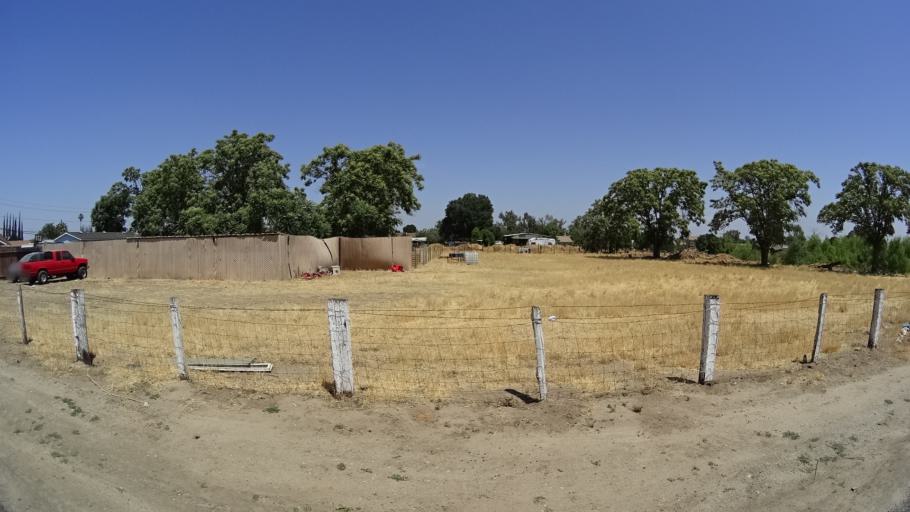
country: US
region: California
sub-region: Kings County
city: Armona
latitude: 36.3057
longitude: -119.7082
